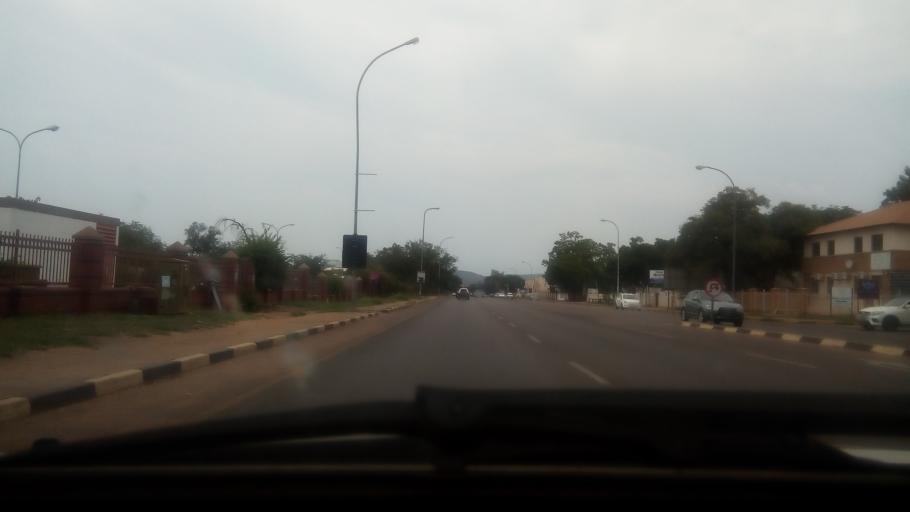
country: BW
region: South East
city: Gaborone
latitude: -24.6591
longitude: 25.9292
